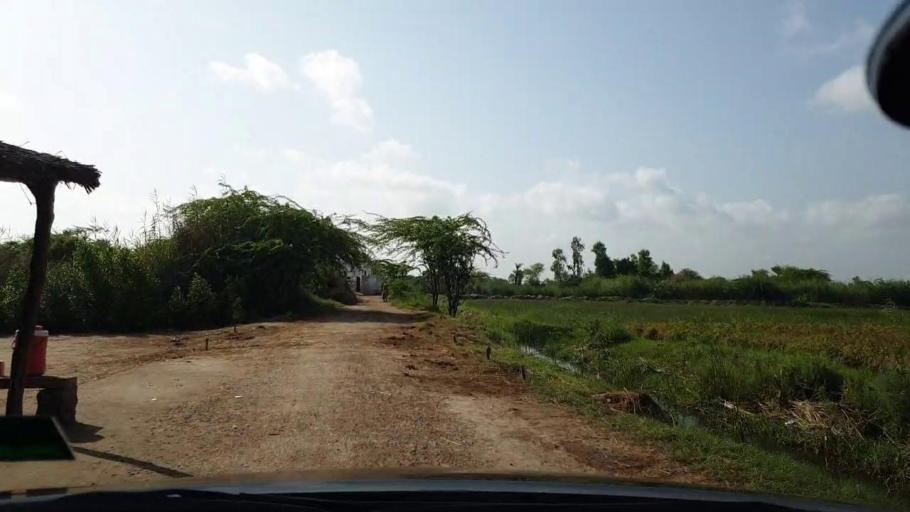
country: PK
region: Sindh
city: Tando Bago
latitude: 24.6443
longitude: 69.0470
